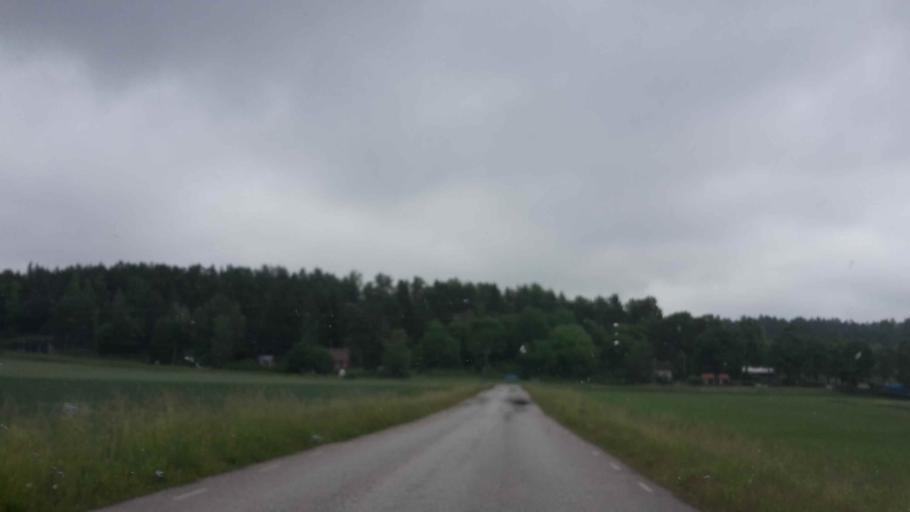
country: SE
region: OEstergoetland
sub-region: Valdemarsviks Kommun
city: Gusum
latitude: 58.3444
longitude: 16.5929
